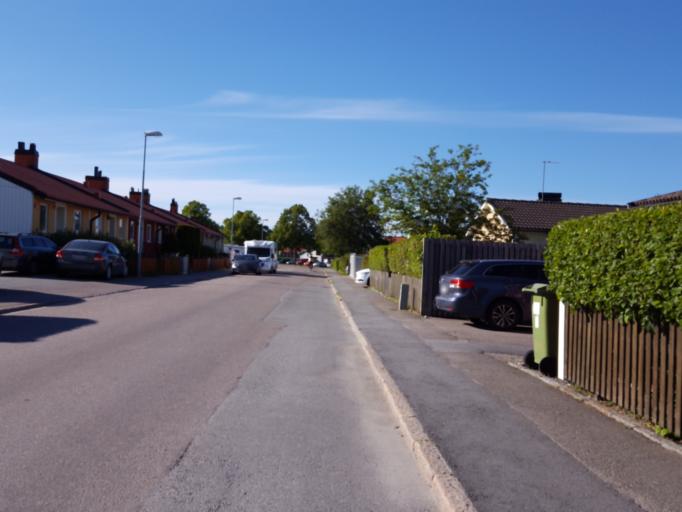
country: SE
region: Uppsala
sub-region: Uppsala Kommun
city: Uppsala
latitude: 59.8595
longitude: 17.6796
